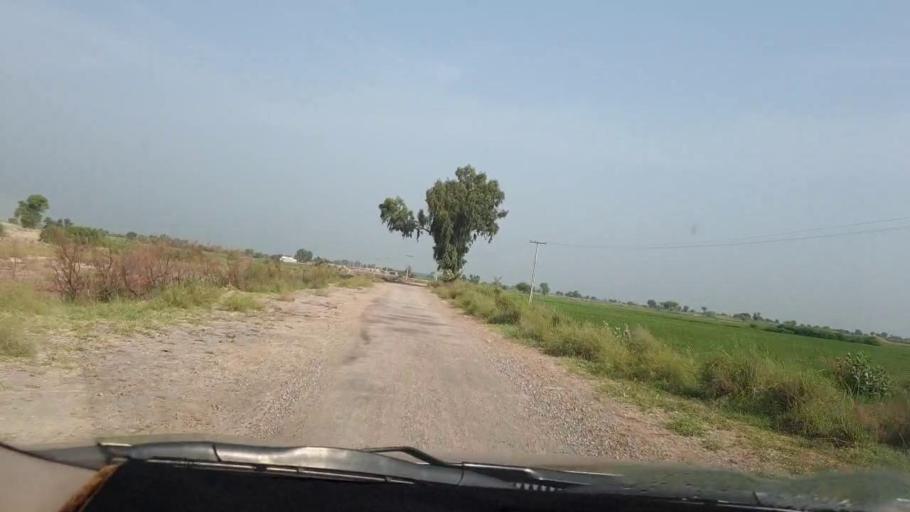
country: PK
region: Sindh
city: Goth Garelo
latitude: 27.4607
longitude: 68.0525
